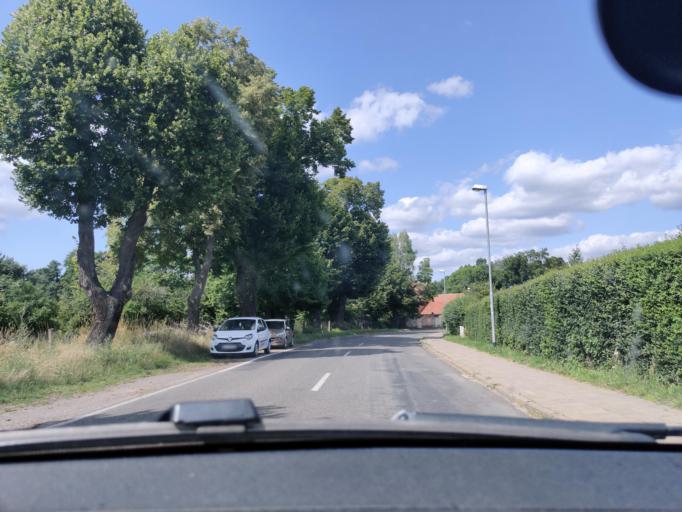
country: DE
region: Saxony-Anhalt
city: Loburg
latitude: 52.1132
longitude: 12.0712
